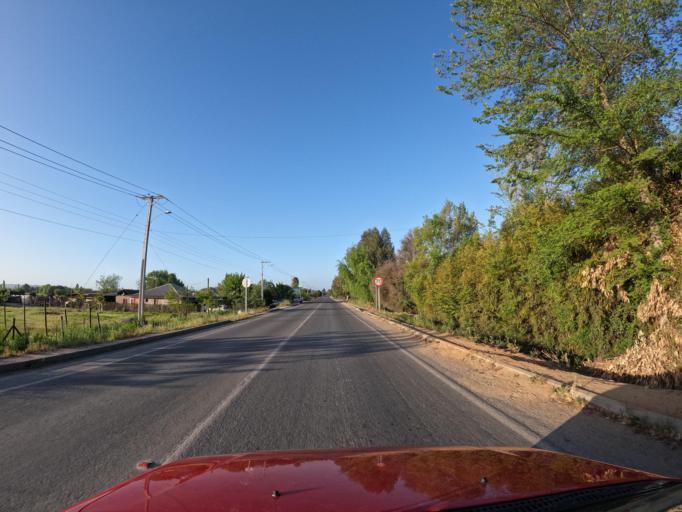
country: CL
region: O'Higgins
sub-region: Provincia de Colchagua
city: Santa Cruz
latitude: -34.3549
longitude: -71.4107
